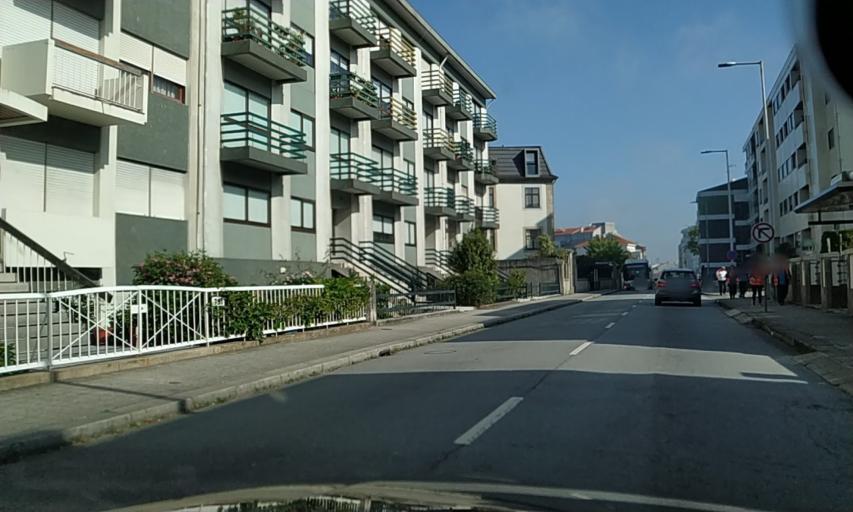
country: PT
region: Porto
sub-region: Porto
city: Porto
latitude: 41.1622
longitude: -8.6247
